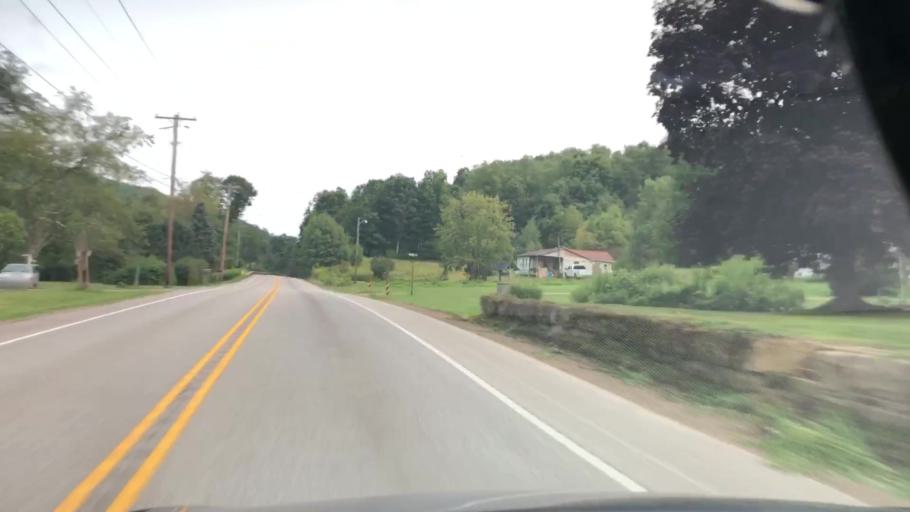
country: US
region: Pennsylvania
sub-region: Venango County
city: Hasson Heights
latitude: 41.5038
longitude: -79.7024
